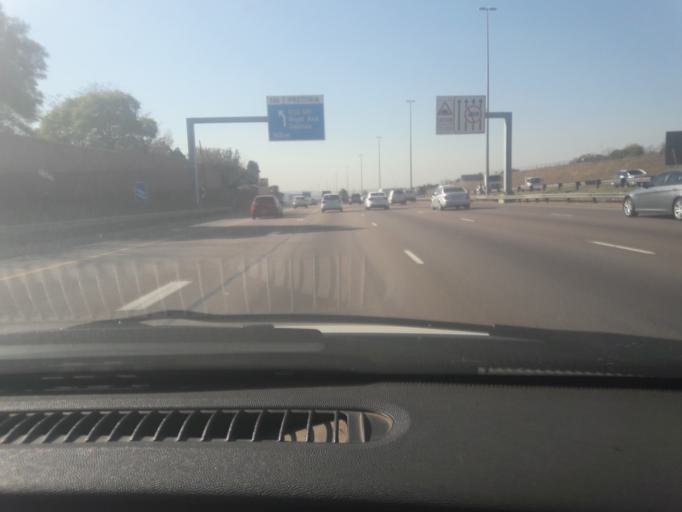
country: ZA
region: Gauteng
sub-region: City of Tshwane Metropolitan Municipality
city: Centurion
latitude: -25.8161
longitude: 28.2554
